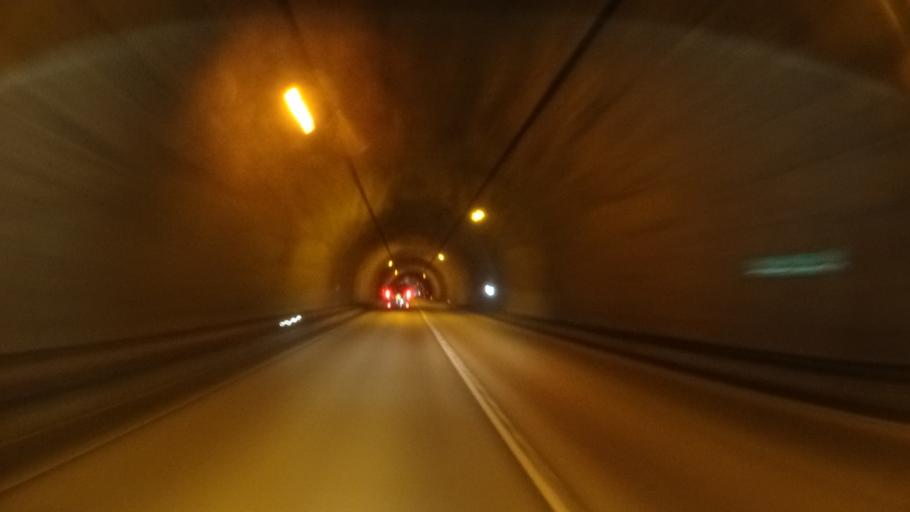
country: JP
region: Ishikawa
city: Nanao
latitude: 37.3300
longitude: 136.8207
